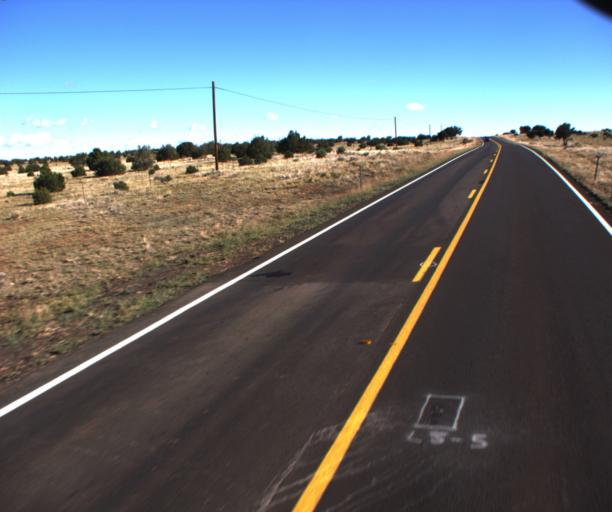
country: US
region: Arizona
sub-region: Apache County
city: Saint Johns
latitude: 34.3996
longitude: -109.6572
